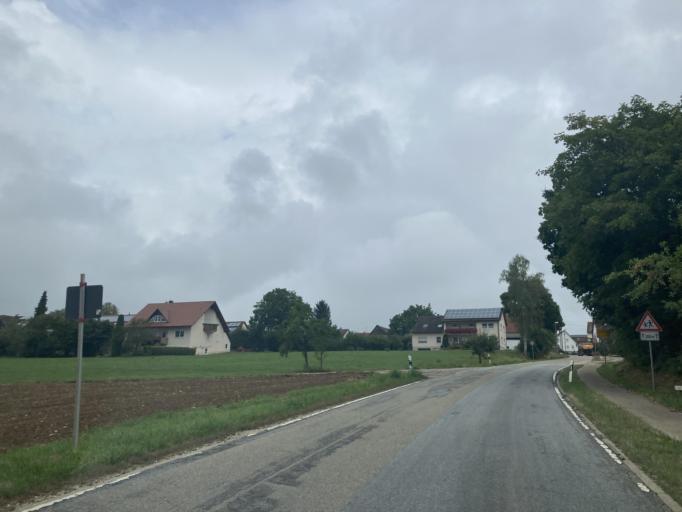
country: DE
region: Baden-Wuerttemberg
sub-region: Regierungsbezirk Stuttgart
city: Dischingen
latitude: 48.7283
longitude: 10.3957
